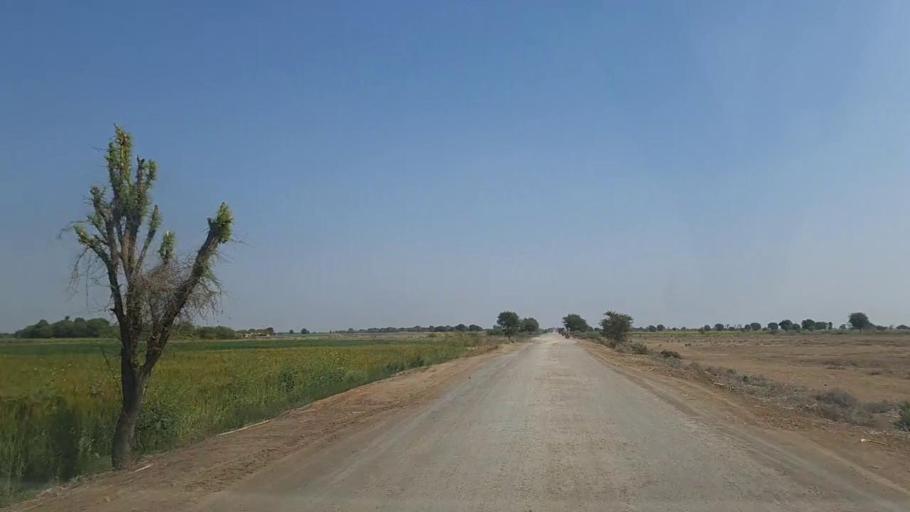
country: PK
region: Sindh
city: Digri
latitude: 25.1673
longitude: 69.1484
